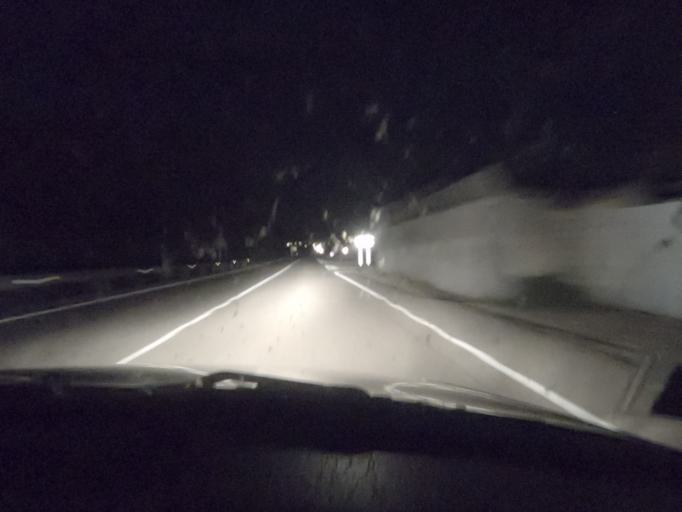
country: ES
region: Castille and Leon
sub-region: Provincia de Salamanca
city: Ciudad Rodrigo
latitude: 40.5800
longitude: -6.5374
